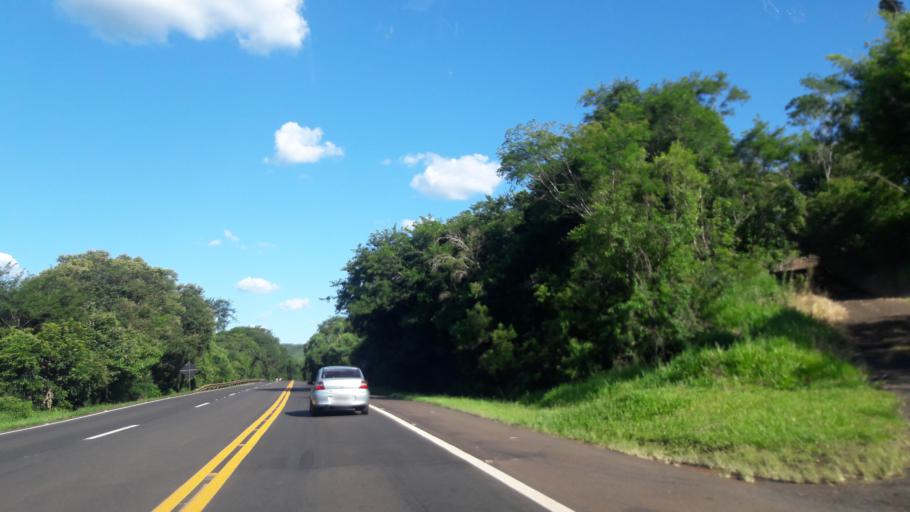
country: BR
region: Parana
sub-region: Laranjeiras Do Sul
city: Laranjeiras do Sul
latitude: -25.4151
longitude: -52.0768
